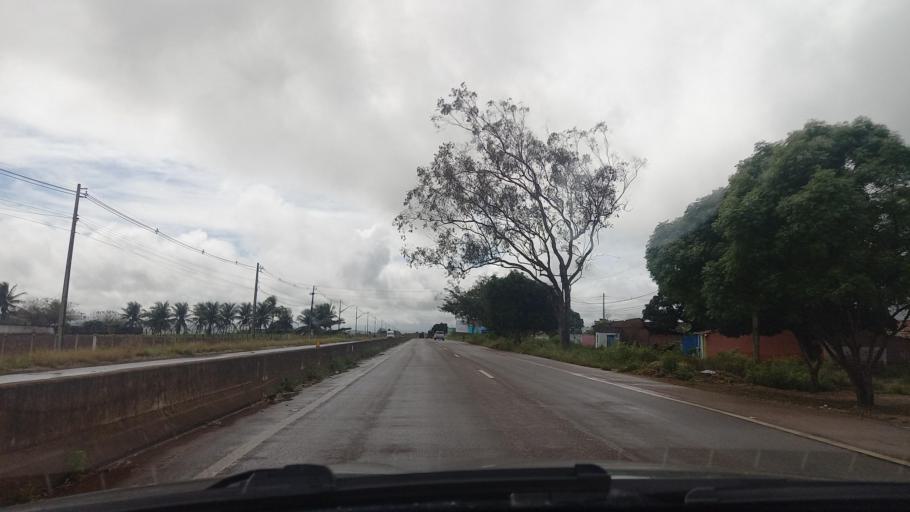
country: BR
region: Alagoas
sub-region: Limoeiro De Anadia
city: Limoeiro de Anadia
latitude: -9.7622
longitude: -36.5308
